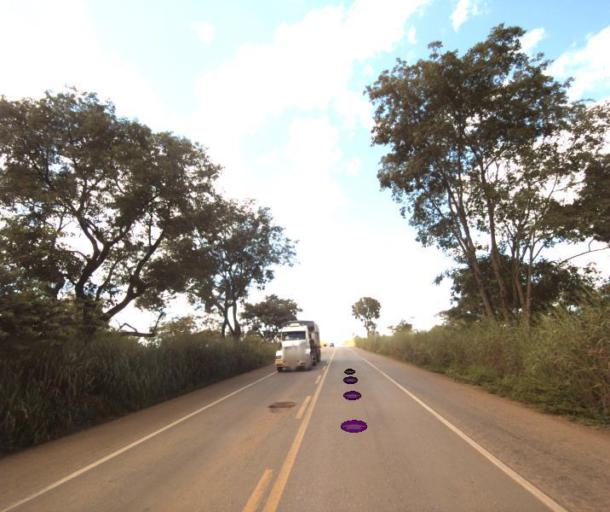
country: BR
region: Goias
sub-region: Petrolina De Goias
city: Petrolina de Goias
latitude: -16.0092
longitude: -49.1260
